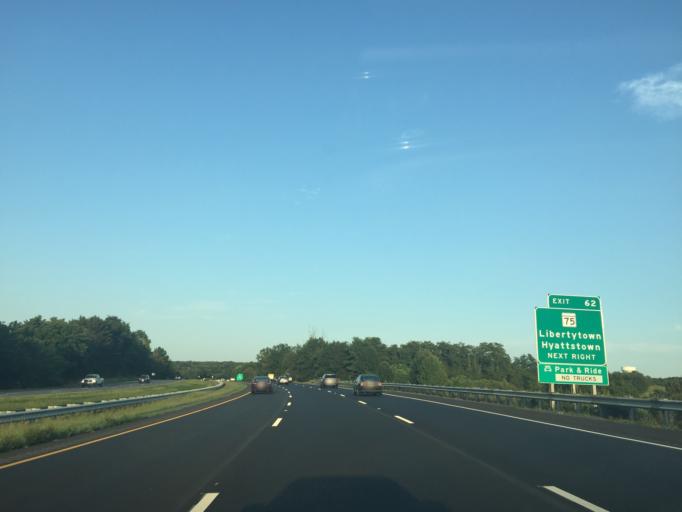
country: US
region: Maryland
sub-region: Frederick County
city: Green Valley
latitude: 39.3804
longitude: -77.2740
